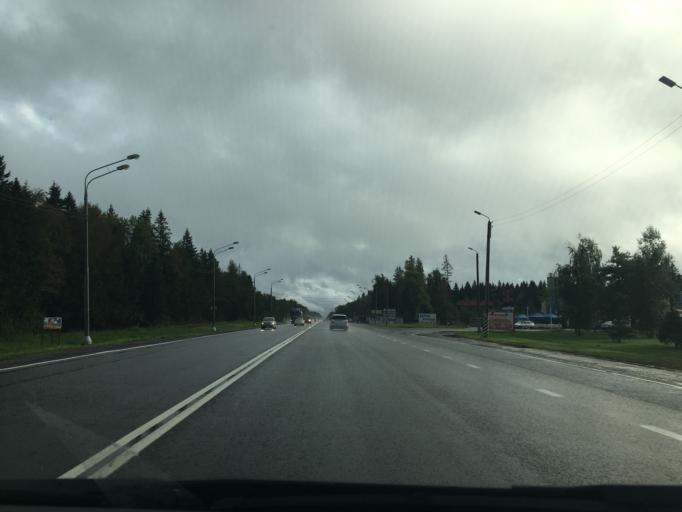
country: RU
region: Kaluga
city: Balabanovo
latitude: 55.1642
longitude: 36.6687
